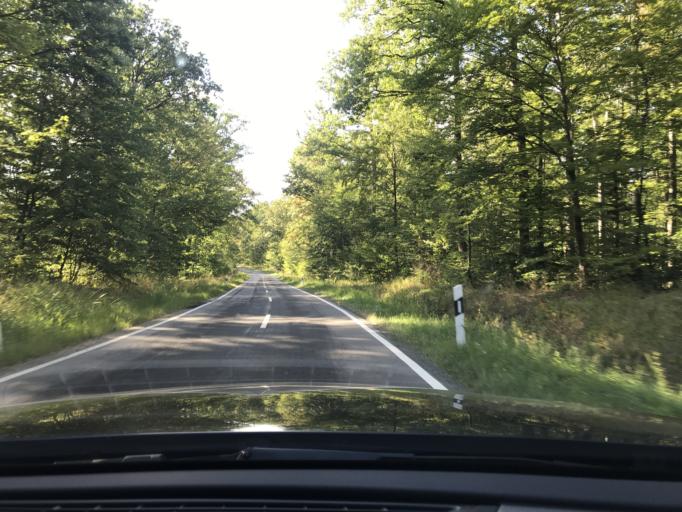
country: DE
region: Bavaria
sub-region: Regierungsbezirk Unterfranken
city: Burgpreppach
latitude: 50.0780
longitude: 10.6556
